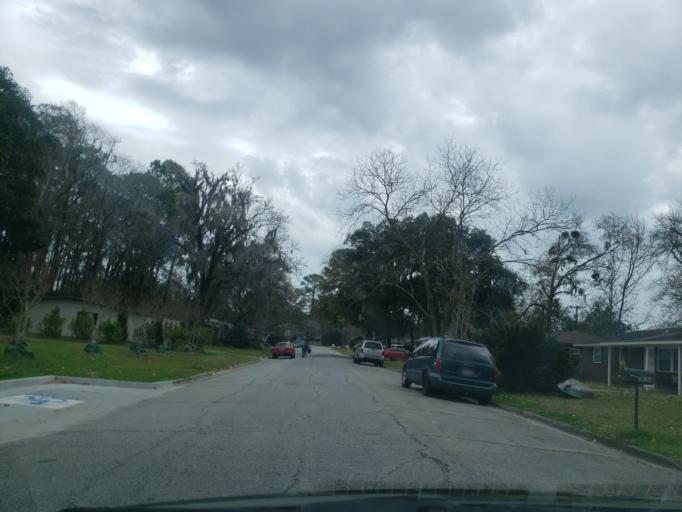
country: US
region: Georgia
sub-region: Chatham County
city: Montgomery
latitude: 31.9947
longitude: -81.1194
